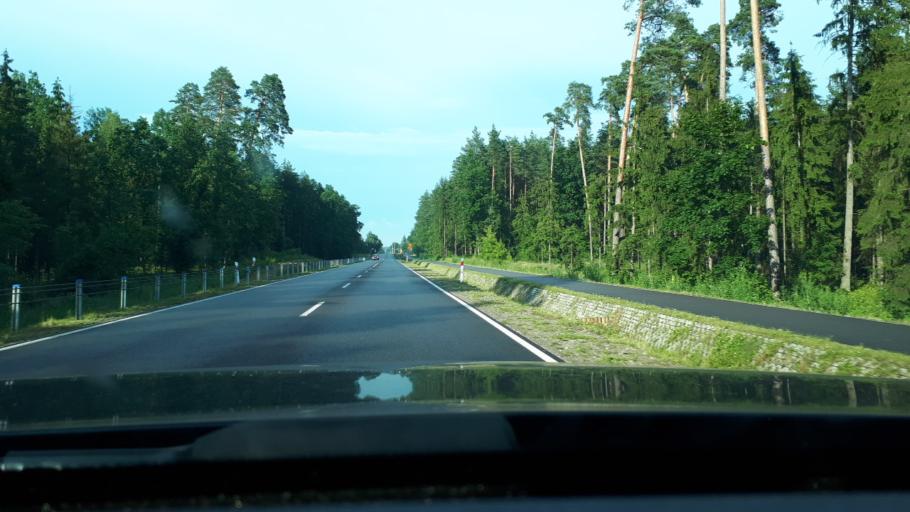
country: PL
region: Podlasie
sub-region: Powiat bialostocki
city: Suprasl
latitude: 53.2043
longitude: 23.3151
